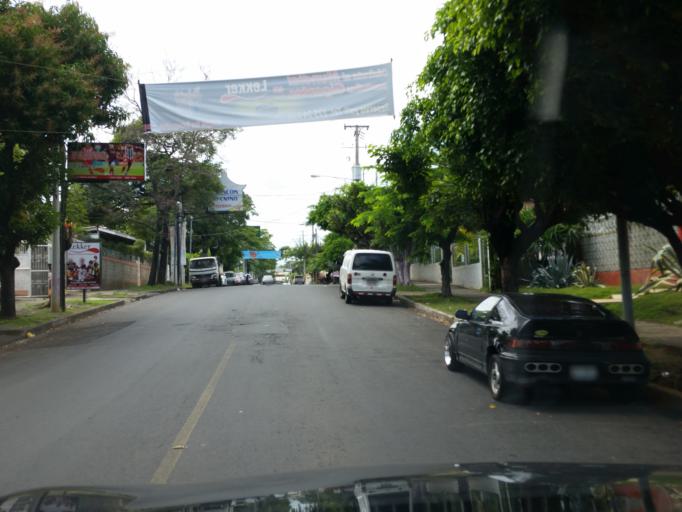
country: NI
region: Managua
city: Managua
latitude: 12.1223
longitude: -86.2597
